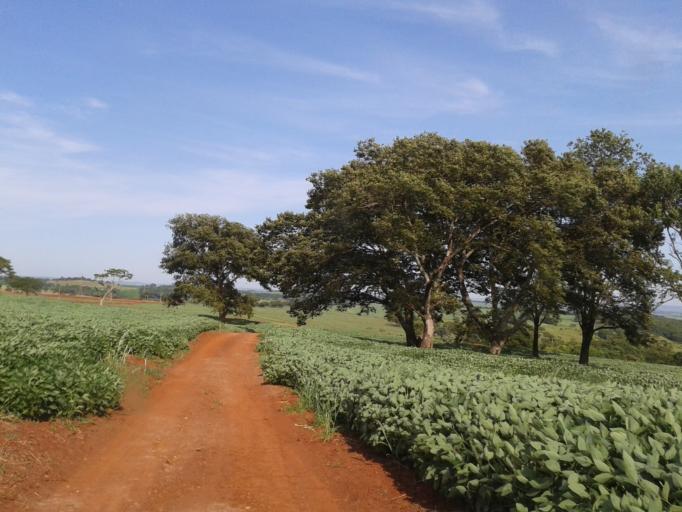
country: BR
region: Minas Gerais
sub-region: Centralina
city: Centralina
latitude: -18.7102
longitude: -49.2056
